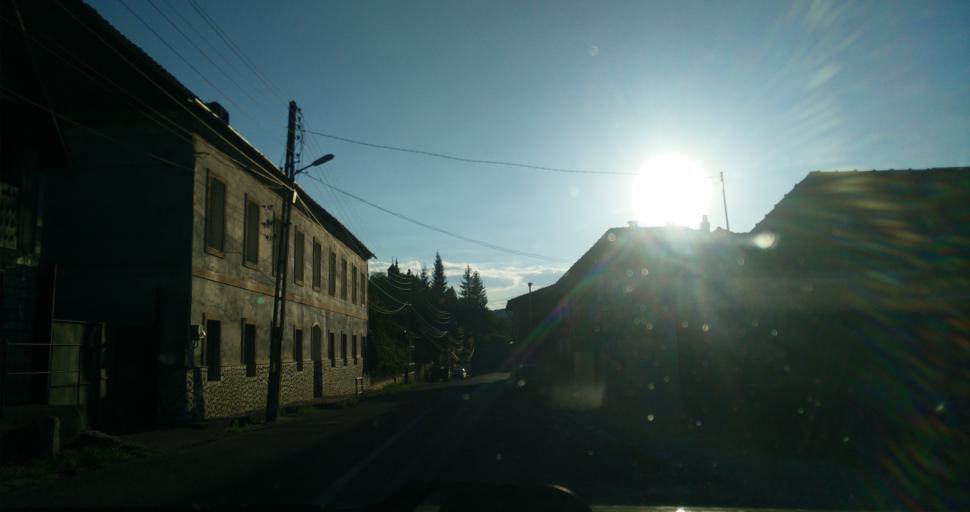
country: RO
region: Bihor
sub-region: Oras Nucet
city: Nucet
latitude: 46.4813
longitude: 22.5838
